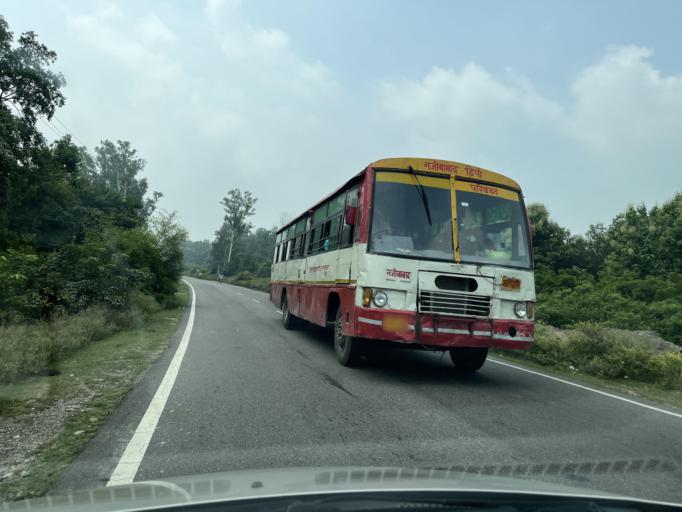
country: IN
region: Uttarakhand
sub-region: Haridwar
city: Sultanpur
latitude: 29.7594
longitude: 78.2687
